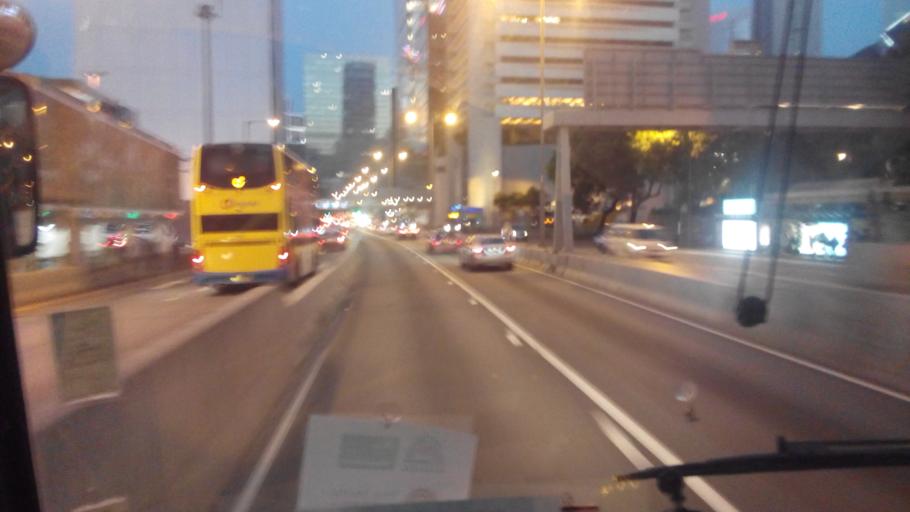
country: HK
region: Central and Western
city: Central
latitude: 22.2821
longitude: 114.1602
